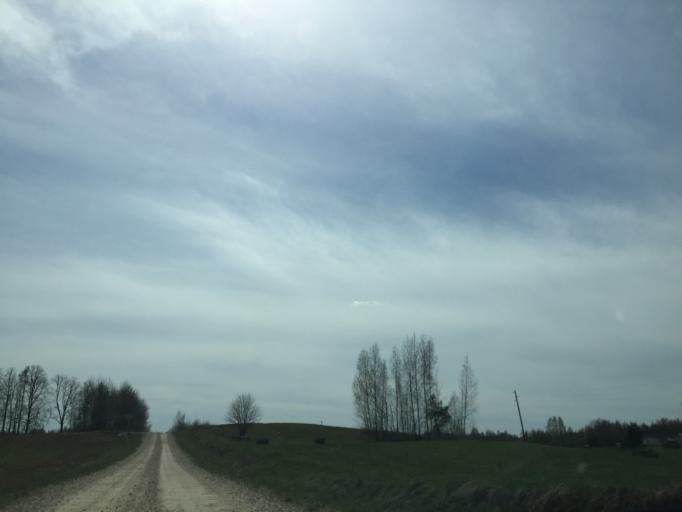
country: LV
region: Ludzas Rajons
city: Ludza
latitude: 56.5434
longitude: 27.5263
